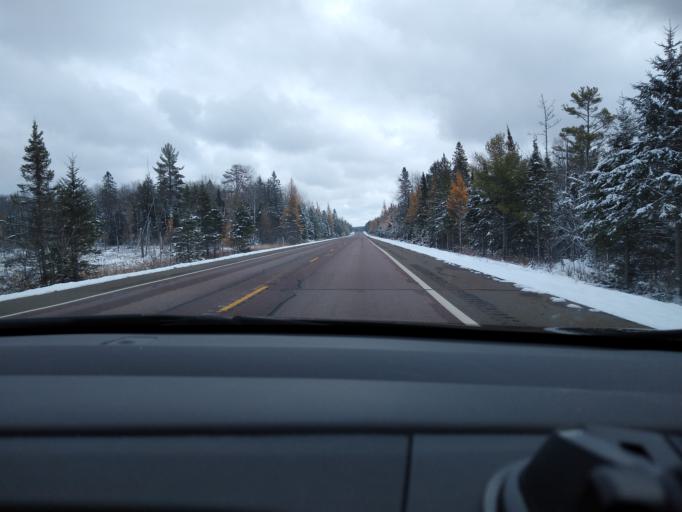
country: US
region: Michigan
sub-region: Iron County
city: Iron River
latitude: 46.1675
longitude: -88.9196
